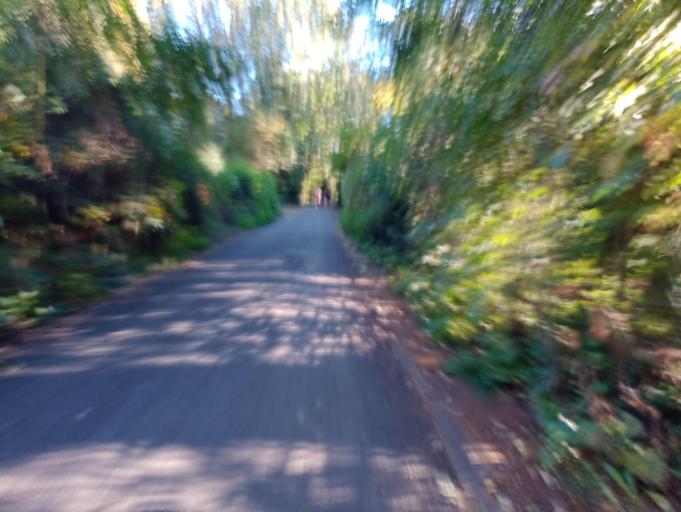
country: DE
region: Hesse
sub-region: Regierungsbezirk Darmstadt
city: Frankfurt am Main
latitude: 50.1376
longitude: 8.7073
